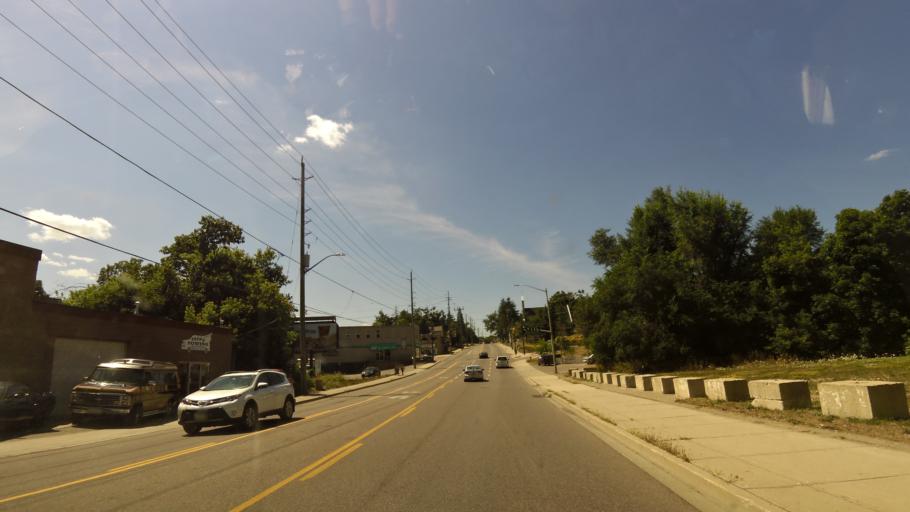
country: CA
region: Ontario
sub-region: Halton
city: Milton
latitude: 43.6513
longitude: -79.9235
